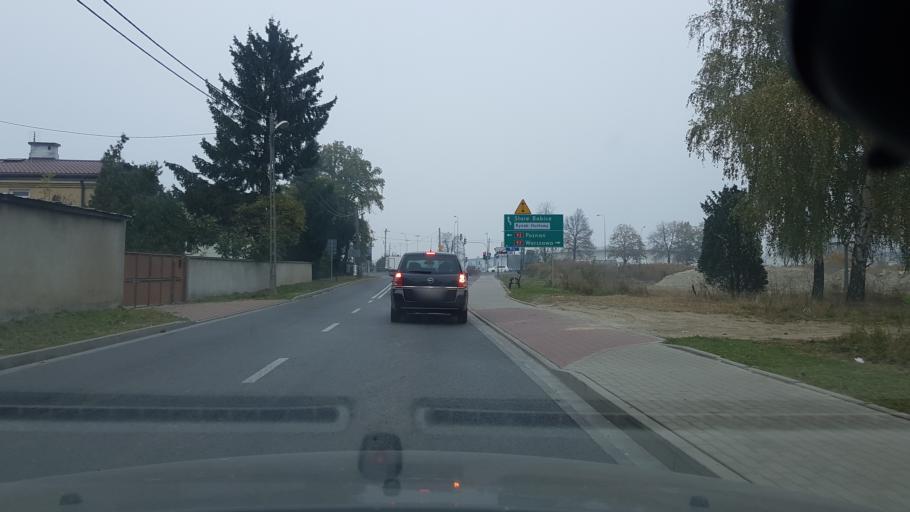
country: PL
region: Masovian Voivodeship
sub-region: Powiat pruszkowski
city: Piastow
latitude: 52.2133
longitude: 20.8398
